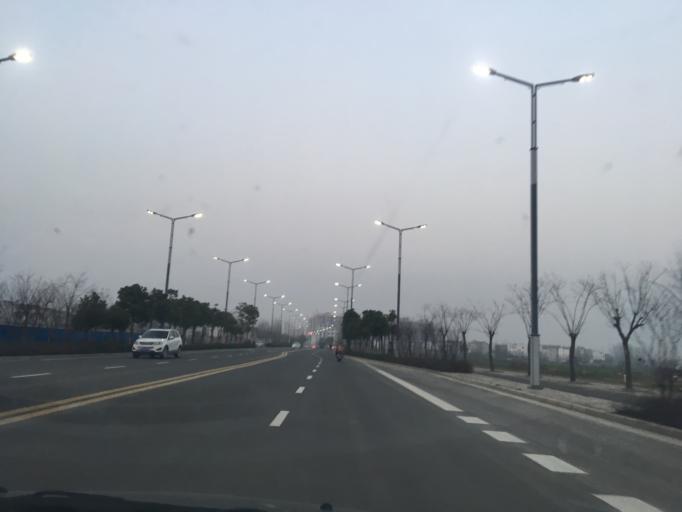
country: CN
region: Hubei
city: Gulou
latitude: 31.1609
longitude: 115.0265
